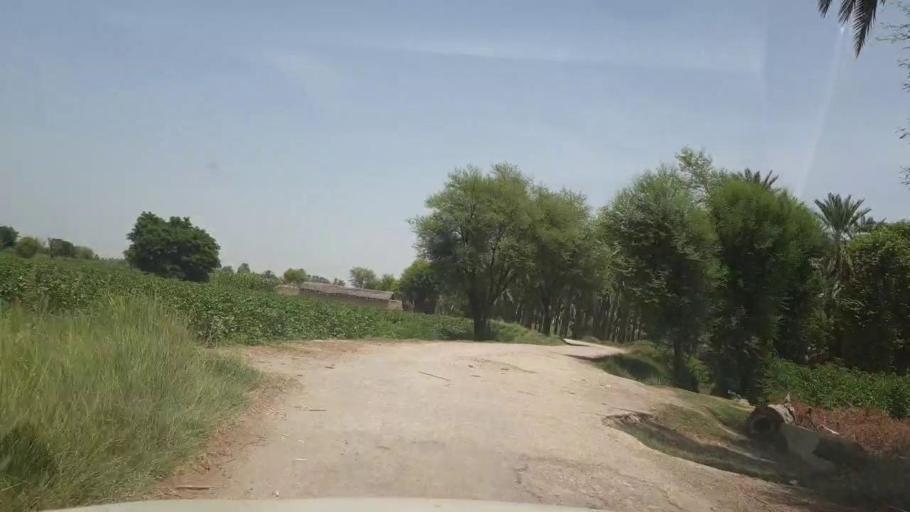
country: PK
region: Sindh
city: Bozdar
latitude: 27.1677
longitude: 68.6228
